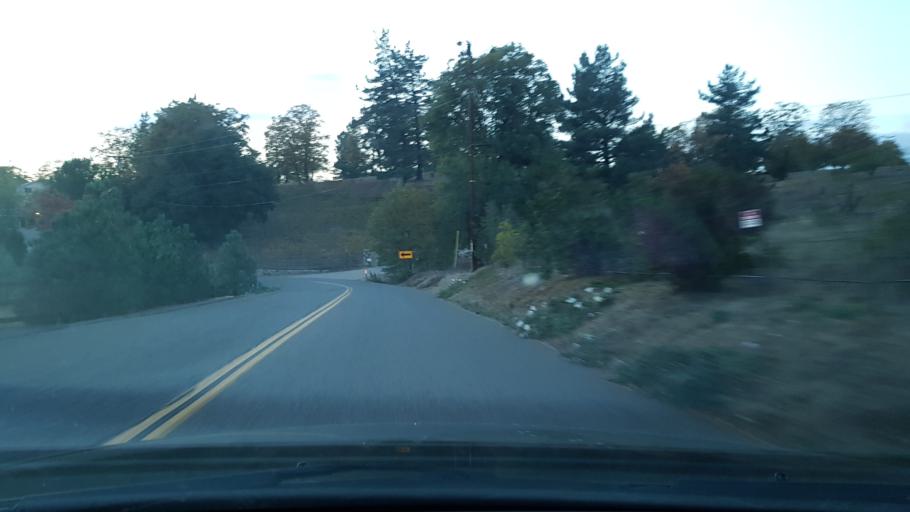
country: US
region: California
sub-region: San Diego County
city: Julian
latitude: 33.1014
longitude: -116.6081
